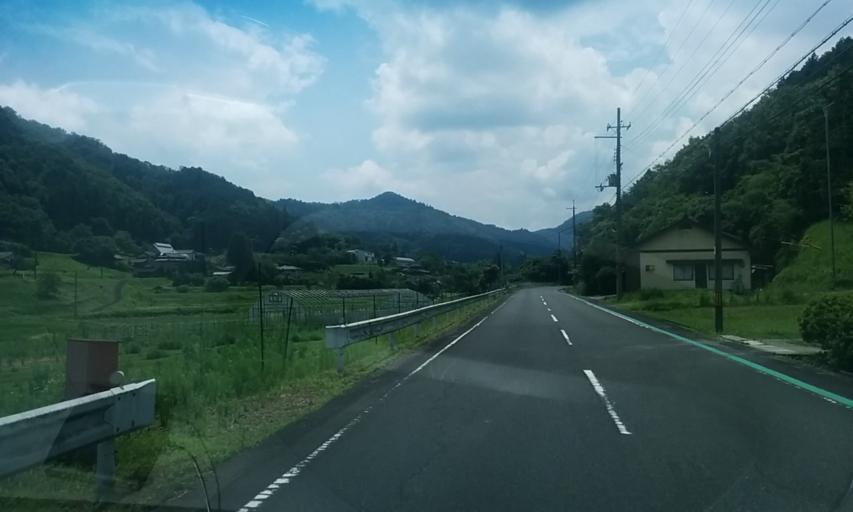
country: JP
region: Kyoto
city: Ayabe
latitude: 35.2076
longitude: 135.2266
